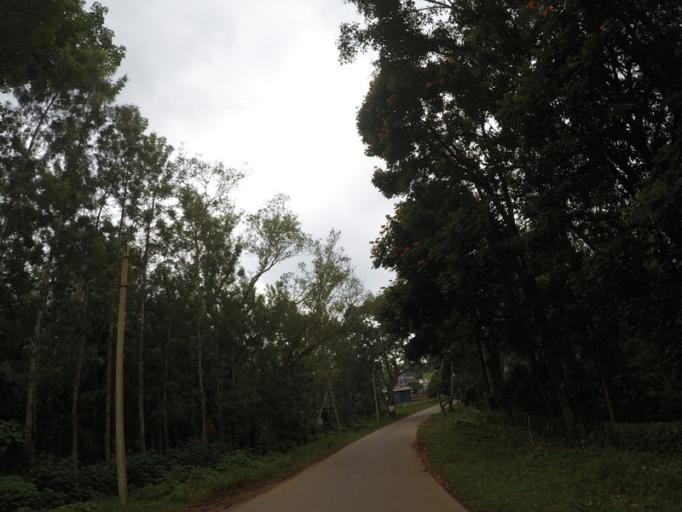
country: IN
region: Karnataka
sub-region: Chikmagalur
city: Chikmagalur
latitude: 13.4849
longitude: 75.8083
